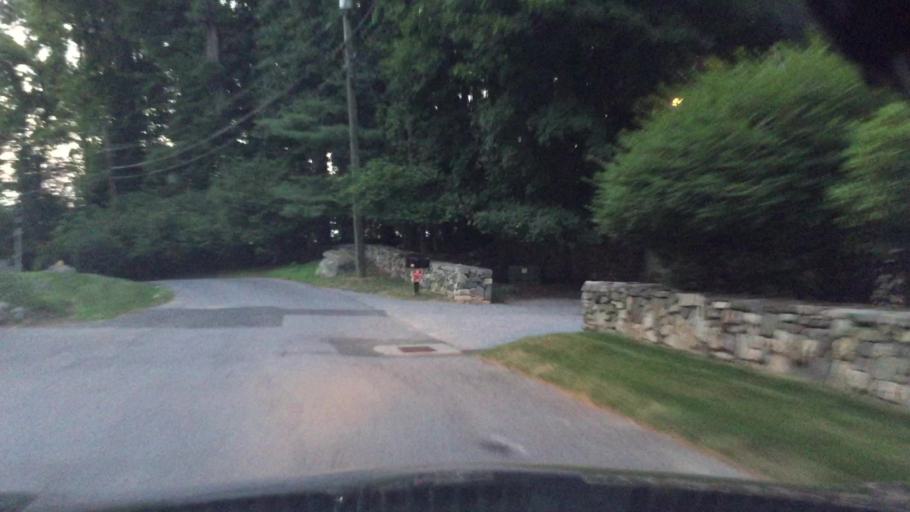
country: US
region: Connecticut
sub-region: Fairfield County
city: East Norwalk
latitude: 41.0755
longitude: -73.4226
